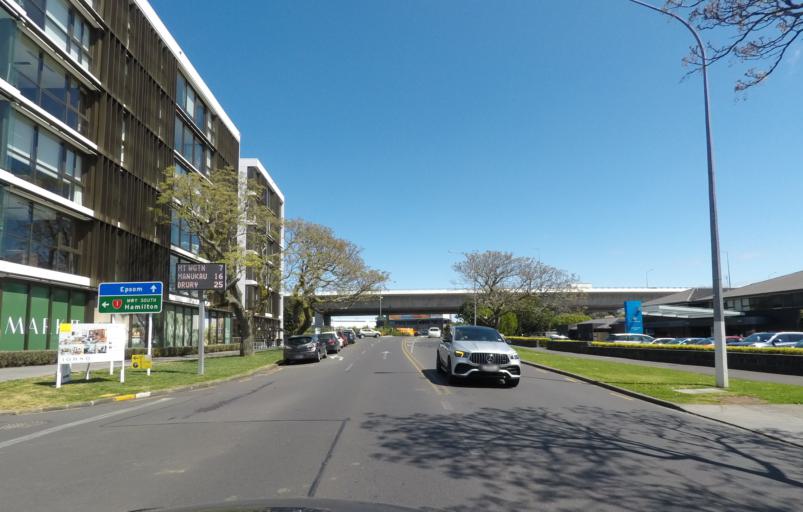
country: NZ
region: Auckland
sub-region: Auckland
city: Auckland
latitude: -36.8740
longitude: 174.7804
